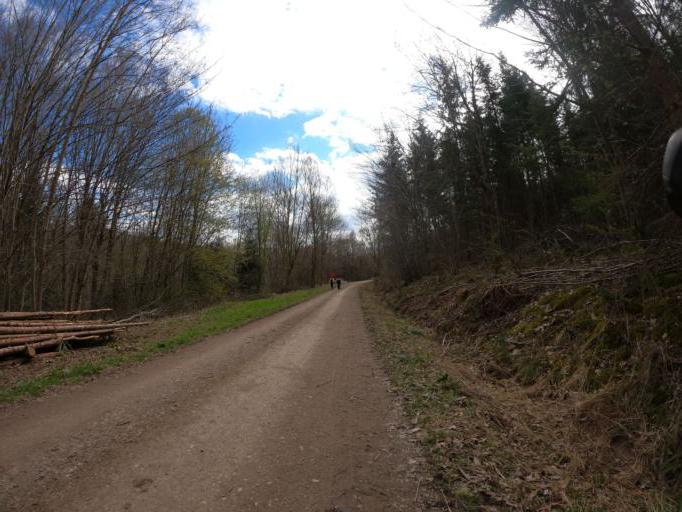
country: DE
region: Baden-Wuerttemberg
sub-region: Tuebingen Region
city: Gomaringen
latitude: 48.4800
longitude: 9.0780
